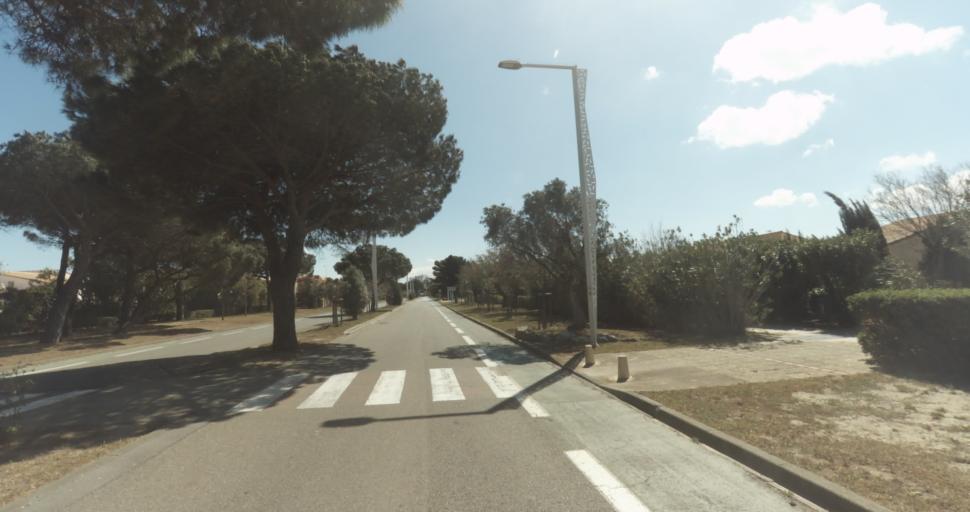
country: FR
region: Languedoc-Roussillon
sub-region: Departement de l'Aude
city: Leucate
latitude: 42.8541
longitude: 3.0407
